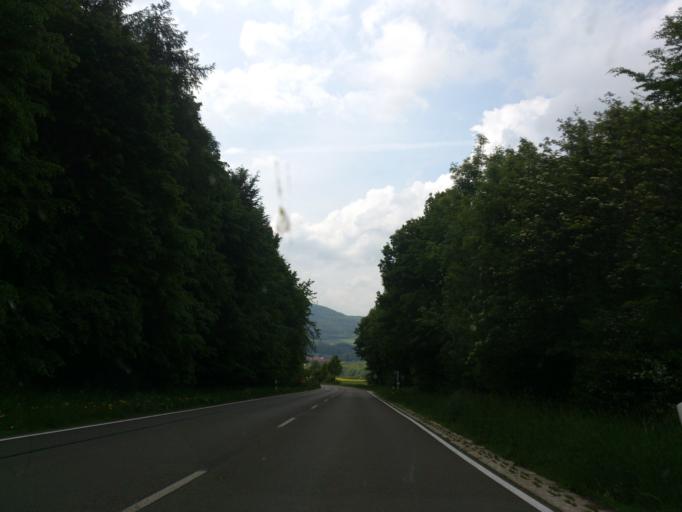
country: DE
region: Hesse
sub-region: Regierungsbezirk Kassel
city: Zierenberg
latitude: 51.3250
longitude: 9.3325
